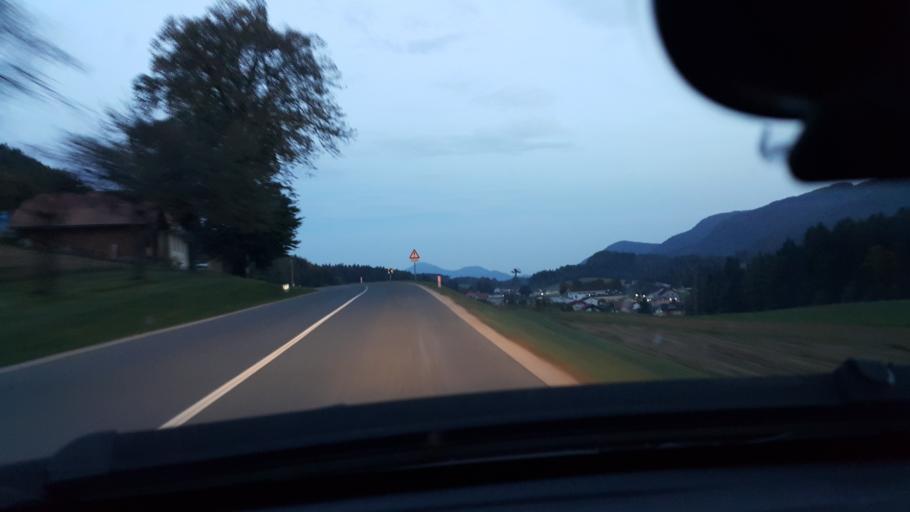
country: SI
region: Zrece
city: Zrece
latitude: 46.3656
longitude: 15.3577
